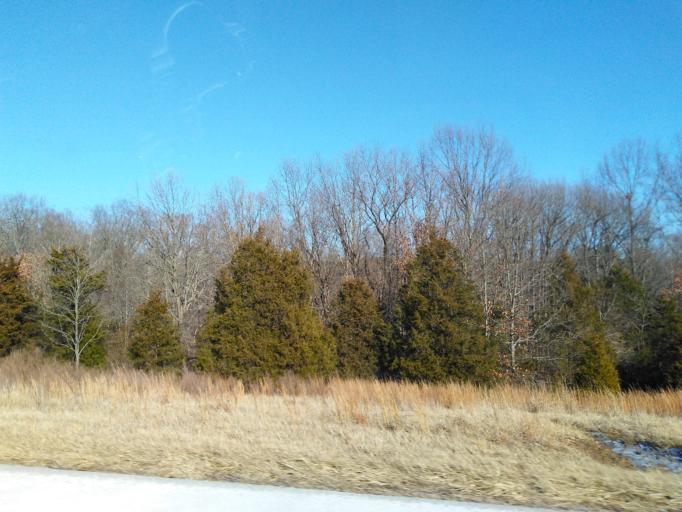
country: US
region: Illinois
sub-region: Johnson County
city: Vienna
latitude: 37.4934
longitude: -88.8943
